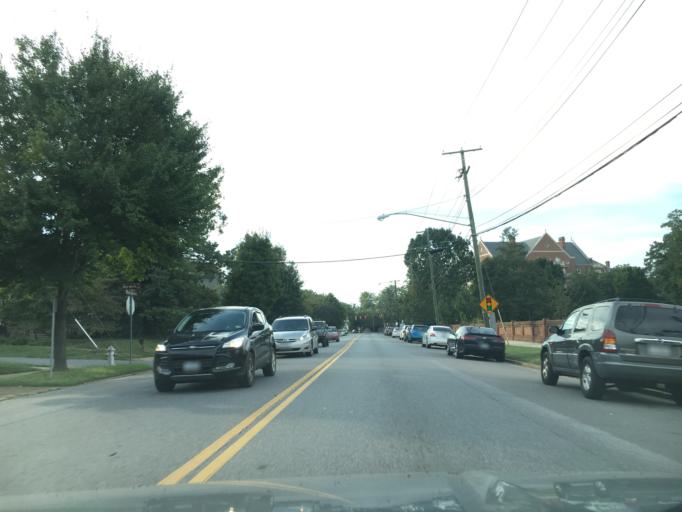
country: US
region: Virginia
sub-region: City of Lynchburg
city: West Lynchburg
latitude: 37.4357
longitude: -79.1722
